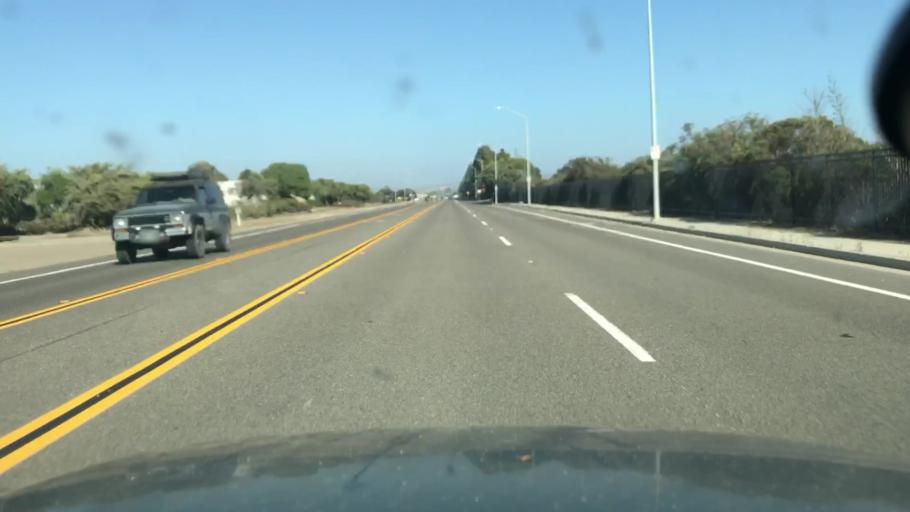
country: US
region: California
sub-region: Santa Barbara County
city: Lompoc
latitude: 34.6610
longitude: -120.4812
